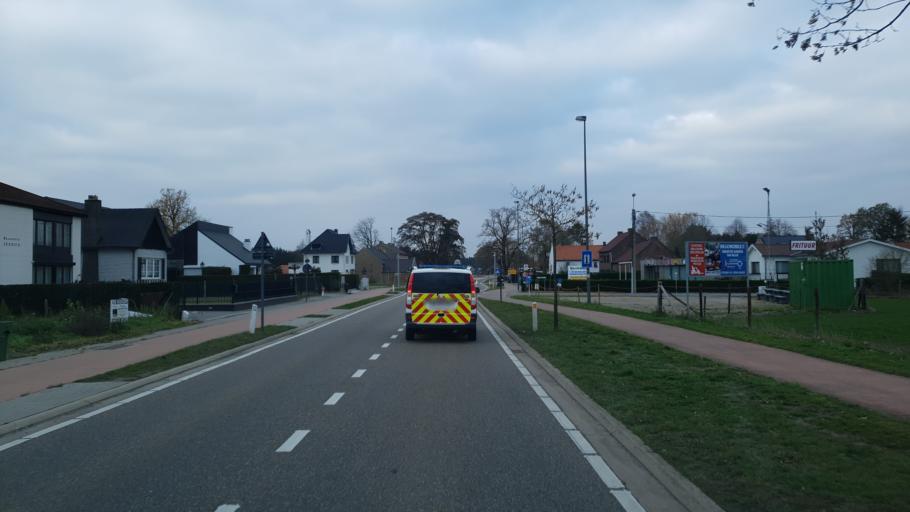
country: BE
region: Flanders
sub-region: Provincie Limburg
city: Zutendaal
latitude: 50.9203
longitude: 5.6082
